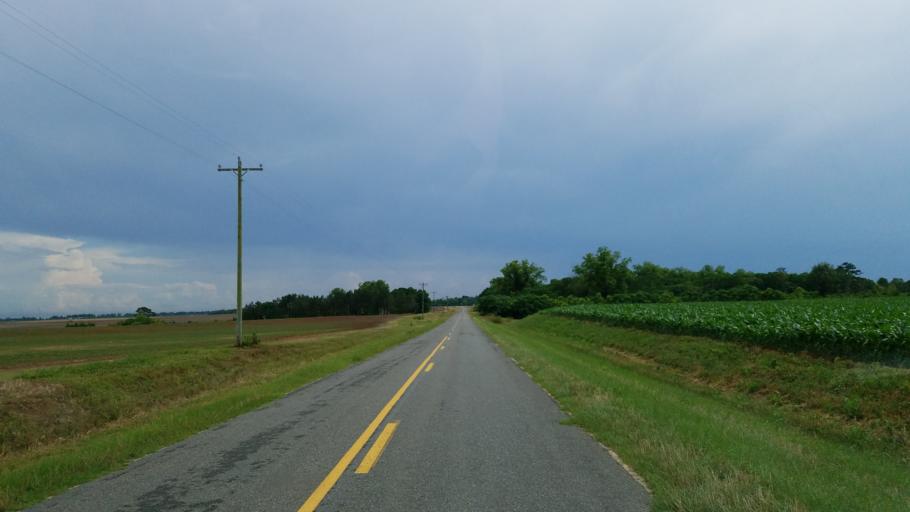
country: US
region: Georgia
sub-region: Dooly County
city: Unadilla
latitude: 32.2867
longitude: -83.7924
